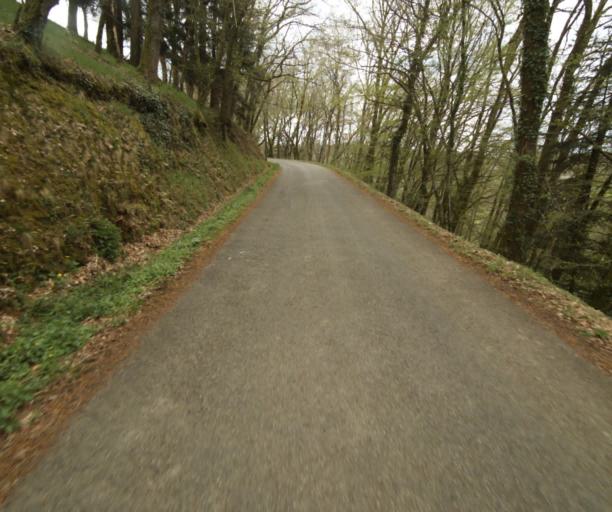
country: FR
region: Limousin
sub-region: Departement de la Correze
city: Laguenne
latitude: 45.2484
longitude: 1.8487
